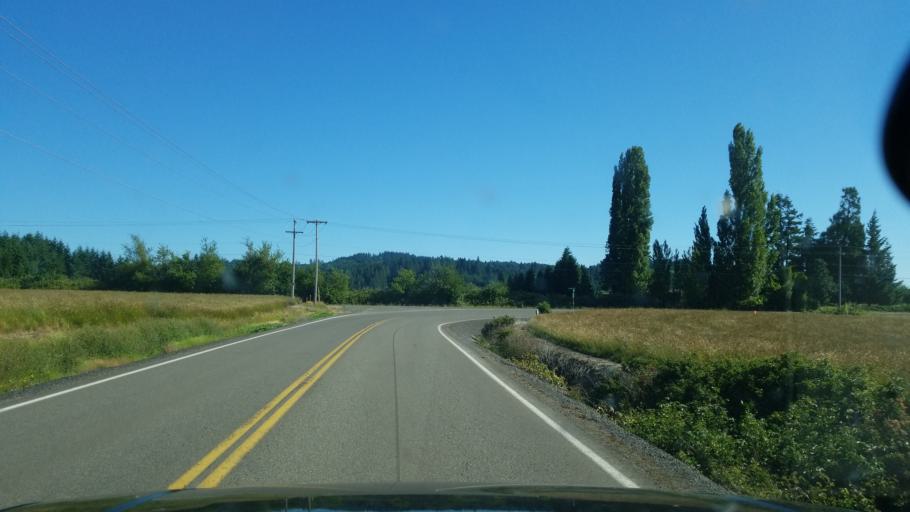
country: US
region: Oregon
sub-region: Yamhill County
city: McMinnville
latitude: 45.2297
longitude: -123.2530
